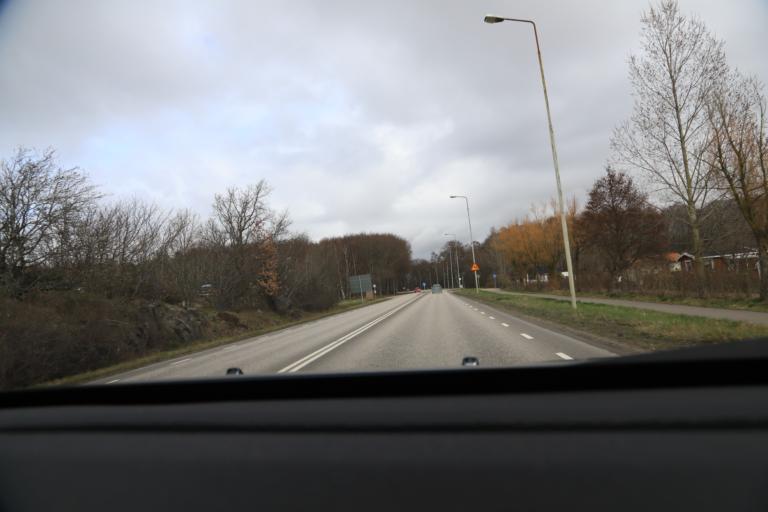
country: SE
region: Halland
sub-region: Varbergs Kommun
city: Varberg
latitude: 57.0937
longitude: 12.2694
